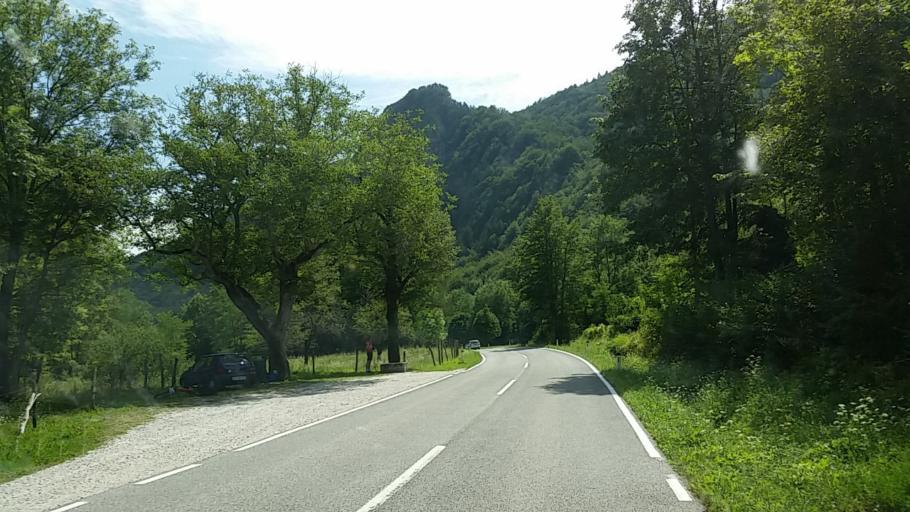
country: SI
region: Bovec
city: Bovec
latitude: 46.2856
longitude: 13.5120
